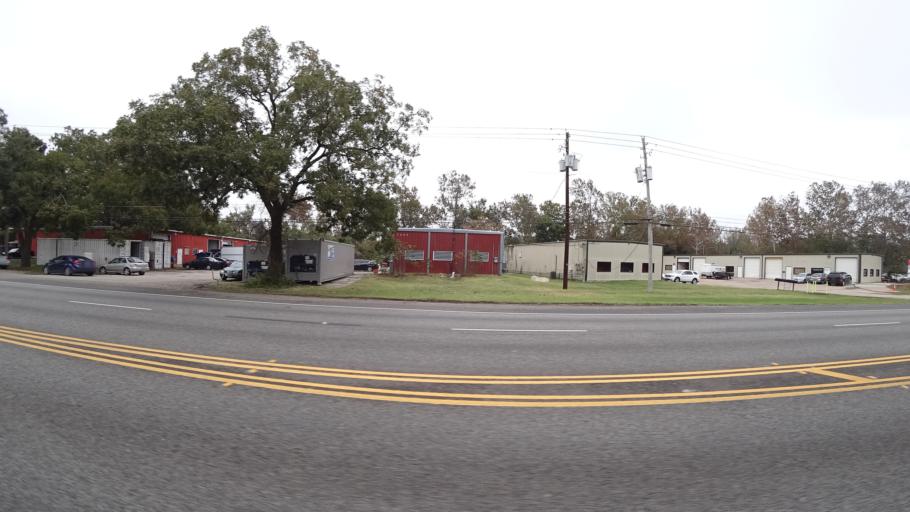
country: US
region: Texas
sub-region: Travis County
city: Barton Creek
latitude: 30.2439
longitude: -97.8841
